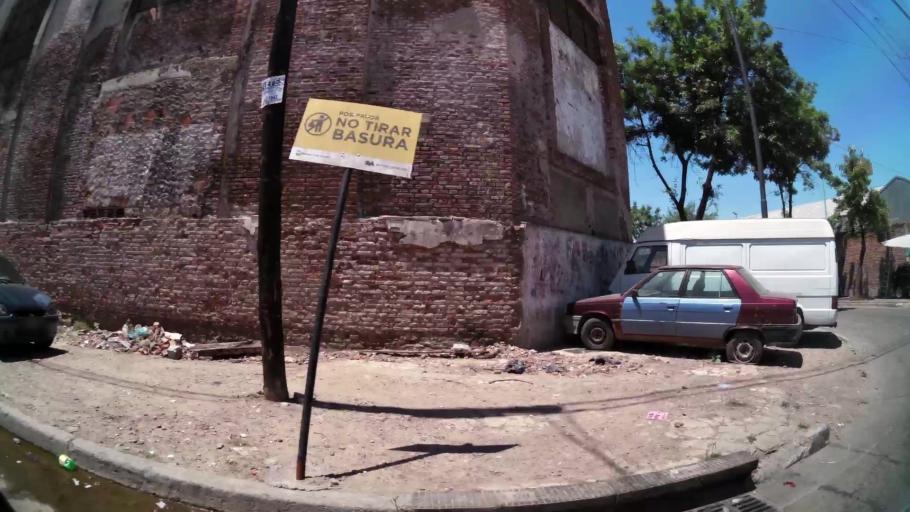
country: AR
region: Buenos Aires
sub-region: Partido de Avellaneda
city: Avellaneda
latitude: -34.6585
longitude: -58.3949
